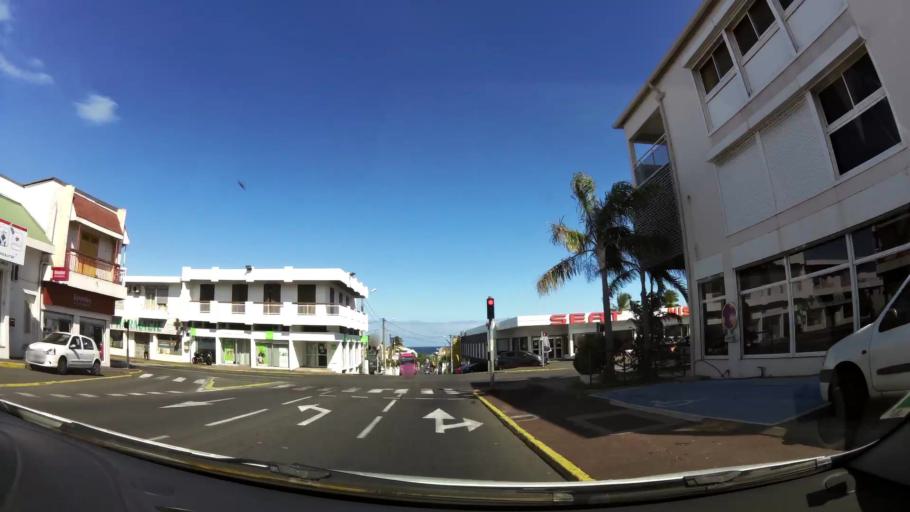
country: RE
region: Reunion
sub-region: Reunion
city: Saint-Pierre
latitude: -21.3362
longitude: 55.4704
